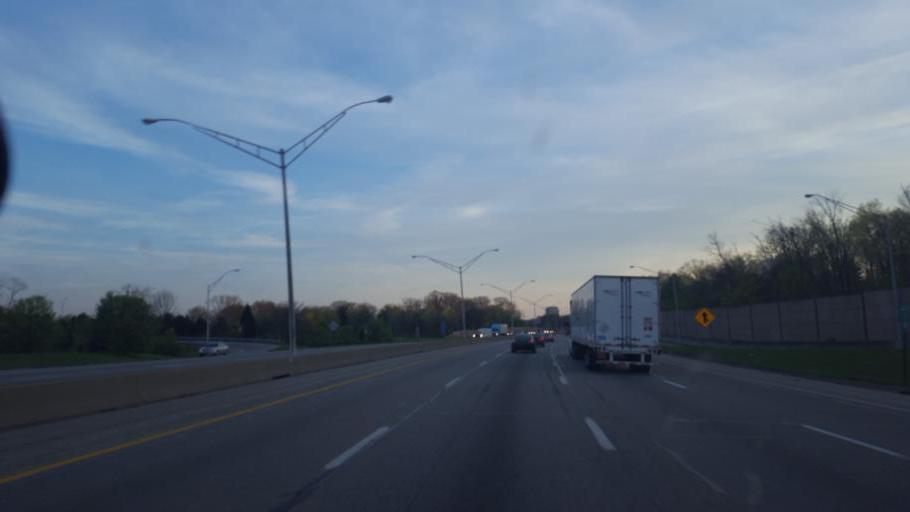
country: US
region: Ohio
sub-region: Hamilton County
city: Blue Ash
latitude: 39.2246
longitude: -84.3671
